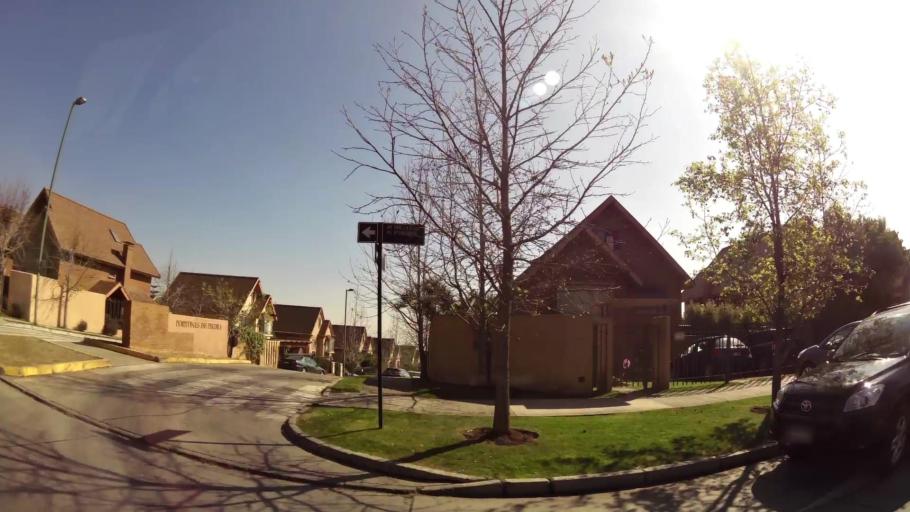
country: CL
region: Santiago Metropolitan
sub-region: Provincia de Santiago
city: Villa Presidente Frei, Nunoa, Santiago, Chile
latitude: -33.4096
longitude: -70.5066
